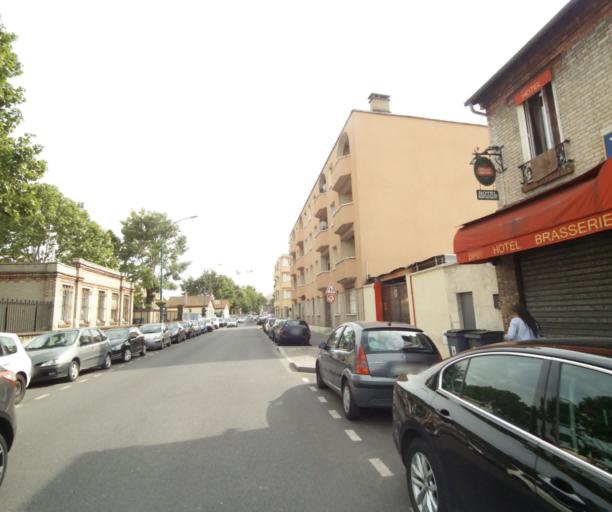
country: FR
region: Ile-de-France
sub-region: Departement des Hauts-de-Seine
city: Gennevilliers
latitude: 48.9292
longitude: 2.2950
